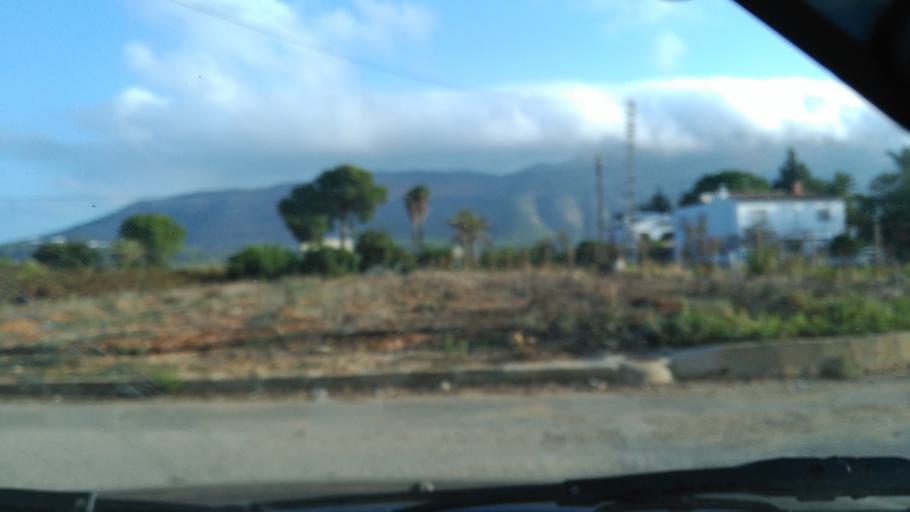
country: ES
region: Valencia
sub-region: Provincia de Alicante
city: Gata de Gorgos
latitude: 38.7862
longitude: 0.0894
